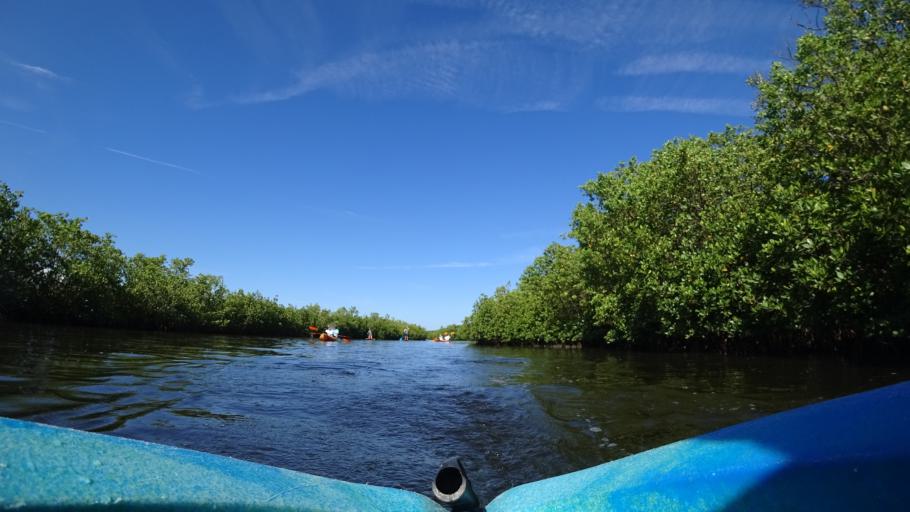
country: US
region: Florida
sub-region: Manatee County
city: Holmes Beach
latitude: 27.5167
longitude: -82.6683
